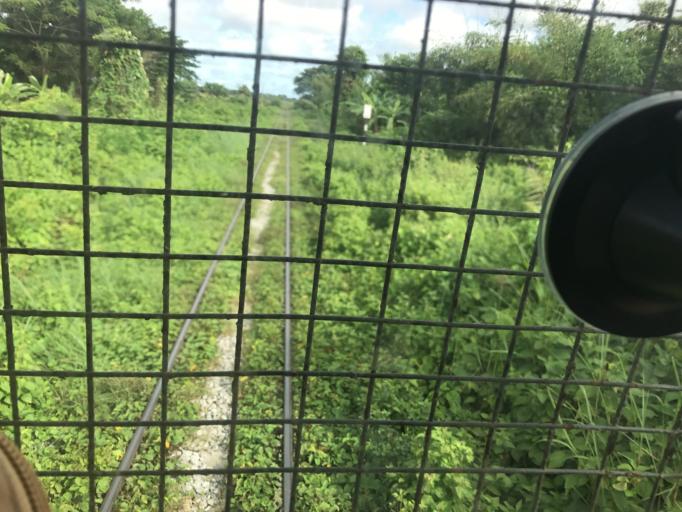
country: MM
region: Bago
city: Letpandan
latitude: 18.0201
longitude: 95.6988
